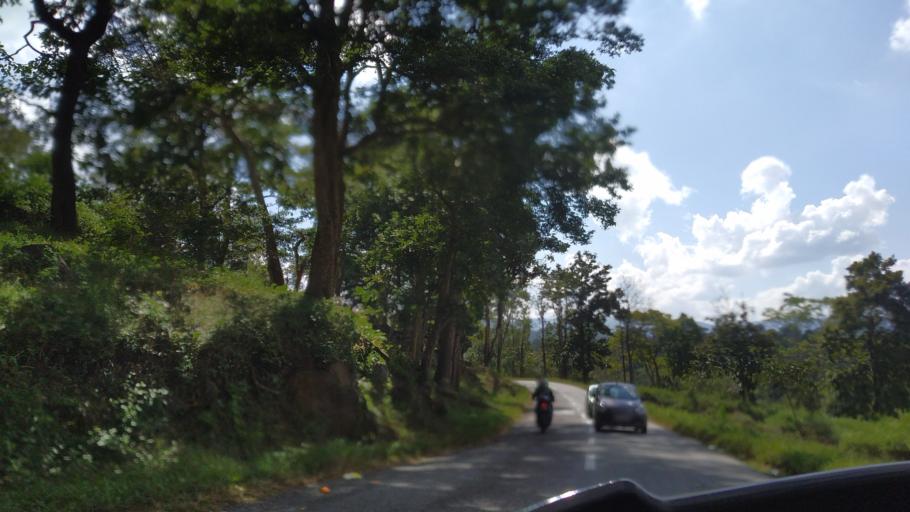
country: IN
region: Kerala
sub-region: Wayanad
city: Panamaram
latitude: 11.9172
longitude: 76.0642
